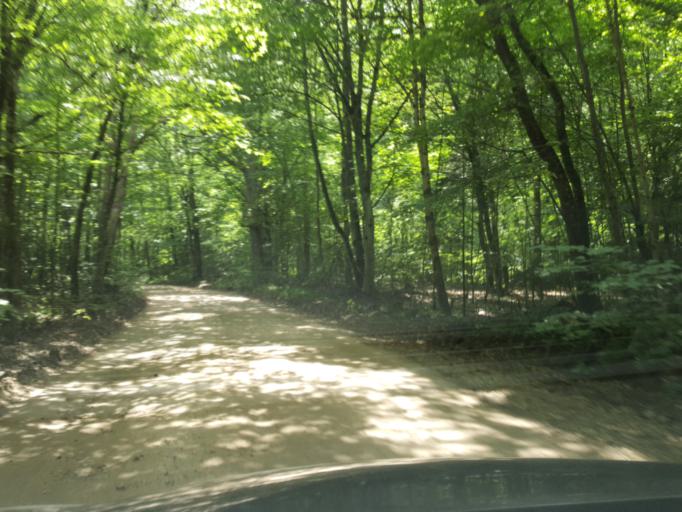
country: LT
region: Alytaus apskritis
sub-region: Alytus
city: Alytus
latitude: 54.3769
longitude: 24.0468
